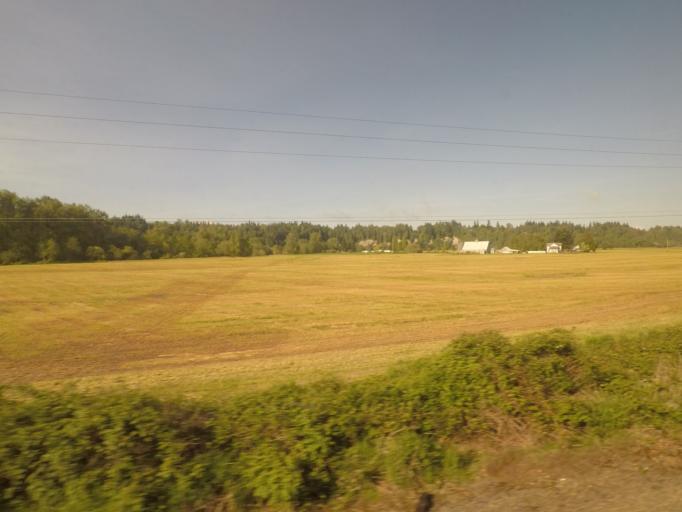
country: US
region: Washington
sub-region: Snohomish County
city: Smokey Point
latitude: 48.1980
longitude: -122.2481
